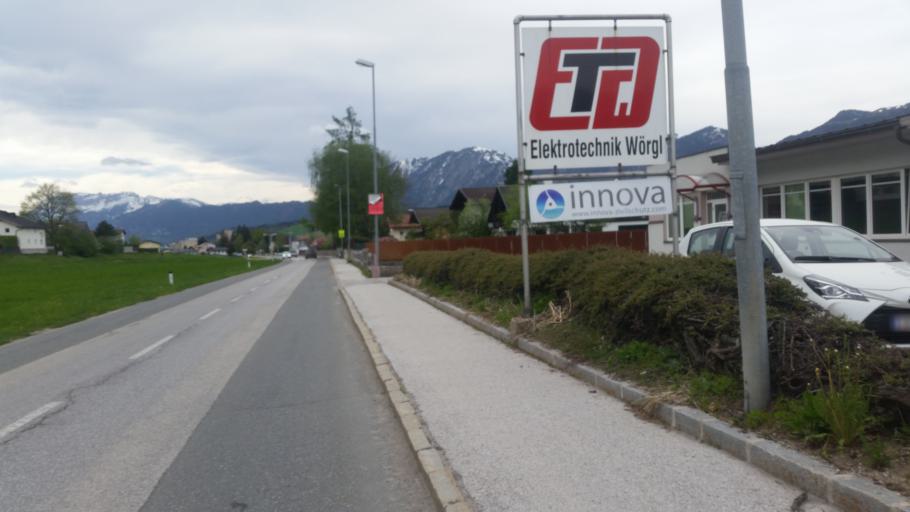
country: AT
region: Tyrol
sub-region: Politischer Bezirk Kufstein
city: Worgl
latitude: 47.4886
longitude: 12.0881
